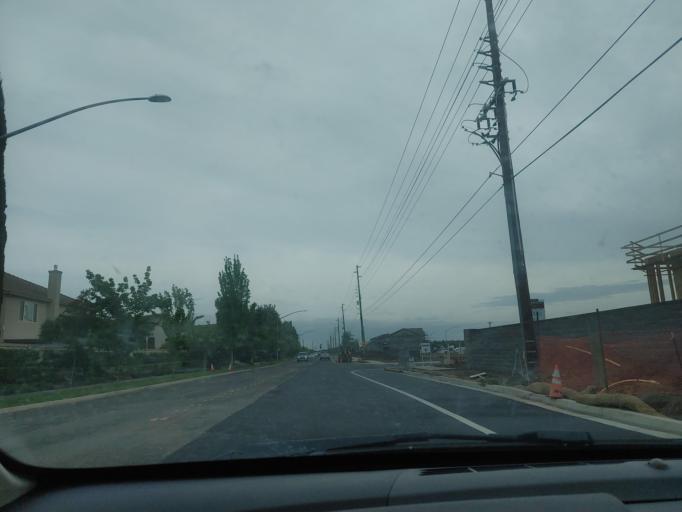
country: US
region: California
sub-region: Stanislaus County
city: Del Rio
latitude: 37.7017
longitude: -121.0226
